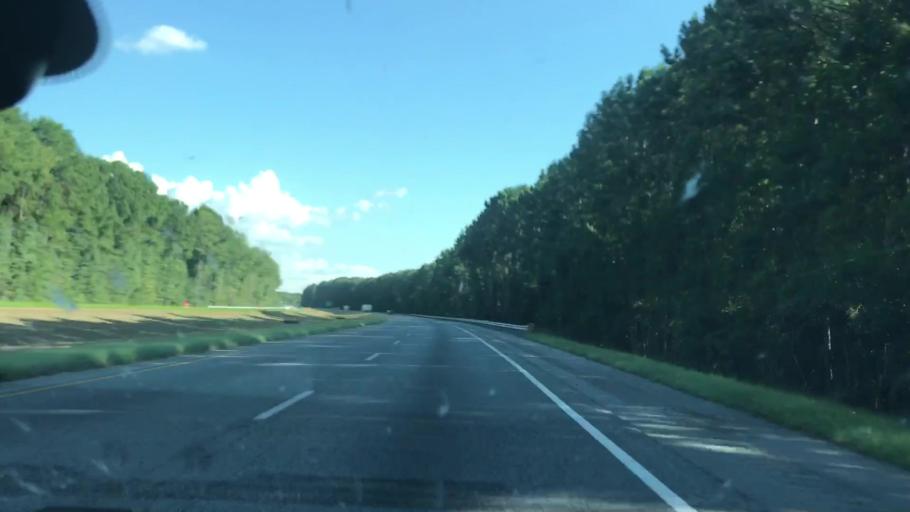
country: US
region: Georgia
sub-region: Harris County
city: Hamilton
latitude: 32.6735
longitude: -84.9884
